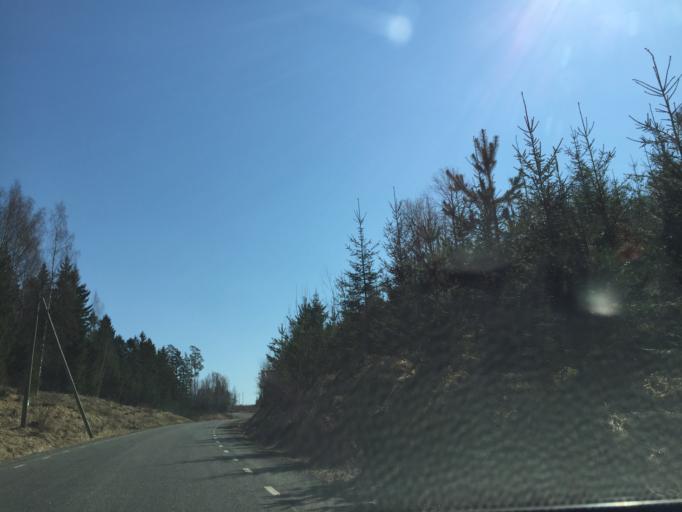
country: EE
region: Tartu
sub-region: Alatskivi vald
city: Kallaste
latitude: 58.5739
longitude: 26.9566
